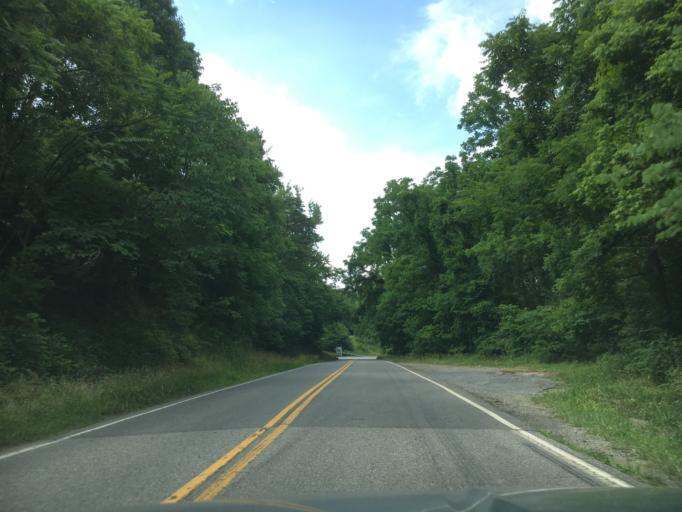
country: US
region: Virginia
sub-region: Roanoke County
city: Cave Spring
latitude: 37.1902
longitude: -80.0022
